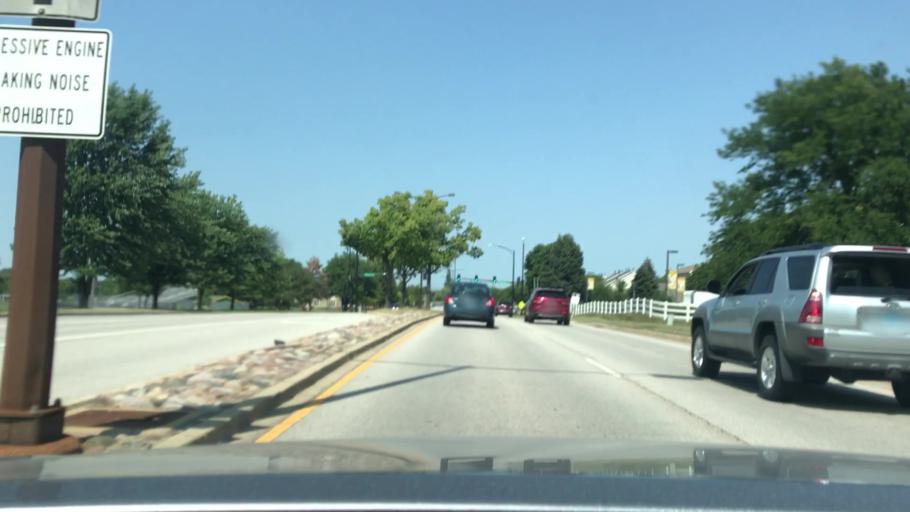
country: US
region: Illinois
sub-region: Kane County
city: Aurora
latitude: 41.7403
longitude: -88.2506
